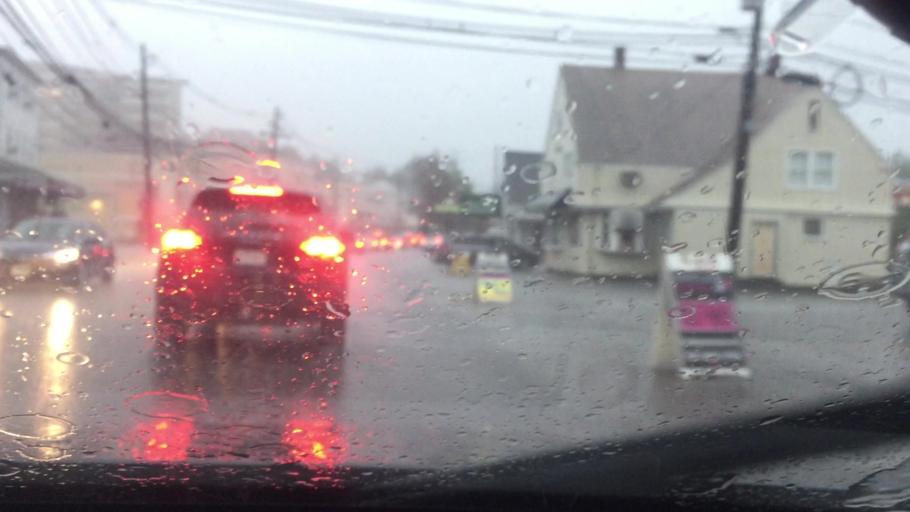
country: US
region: Massachusetts
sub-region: Norfolk County
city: Needham
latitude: 42.3063
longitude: -71.2174
